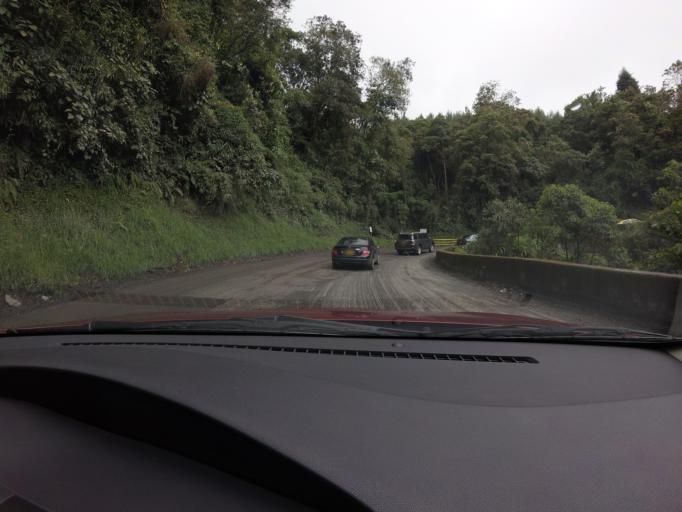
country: CO
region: Tolima
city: Herveo
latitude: 5.1256
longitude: -75.2009
